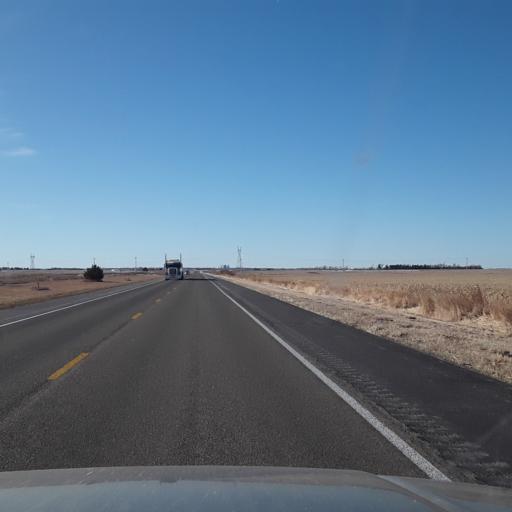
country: US
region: Nebraska
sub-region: Kearney County
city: Minden
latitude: 40.5344
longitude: -98.8705
